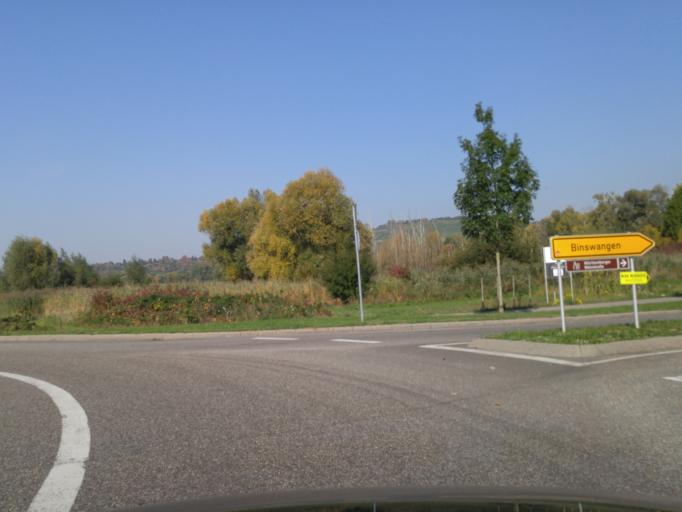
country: DE
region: Baden-Wuerttemberg
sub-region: Regierungsbezirk Stuttgart
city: Erlenbach
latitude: 49.1761
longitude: 9.2506
